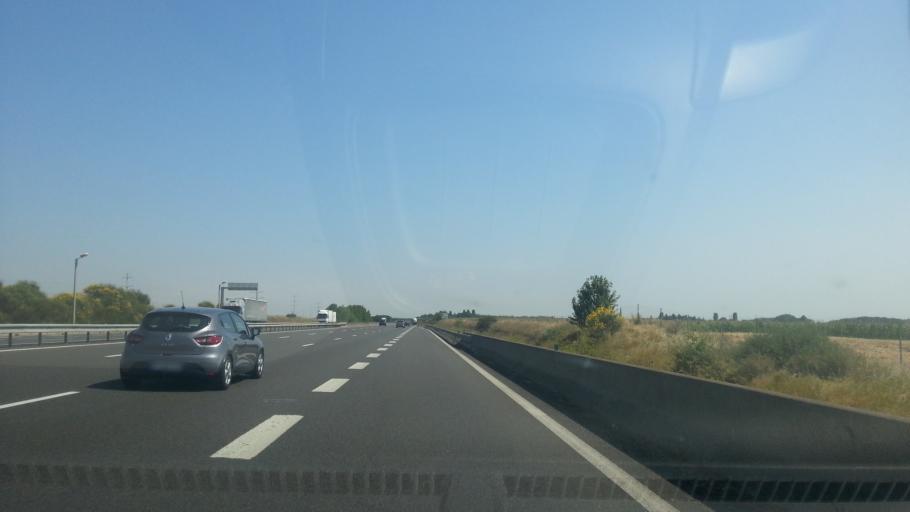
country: FR
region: Centre
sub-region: Departement du Loiret
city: Baule
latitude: 47.8218
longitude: 1.6451
